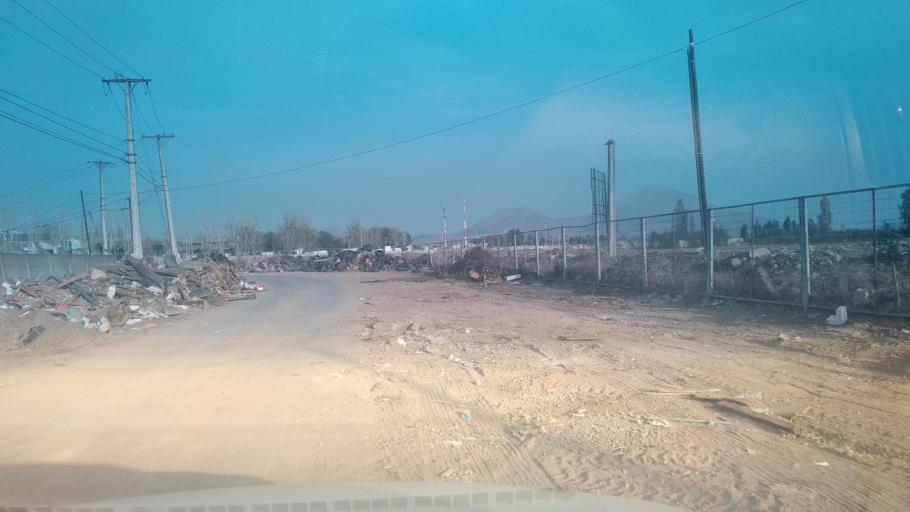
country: CL
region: Santiago Metropolitan
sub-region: Provincia de Chacabuco
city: Chicureo Abajo
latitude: -33.3459
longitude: -70.7194
